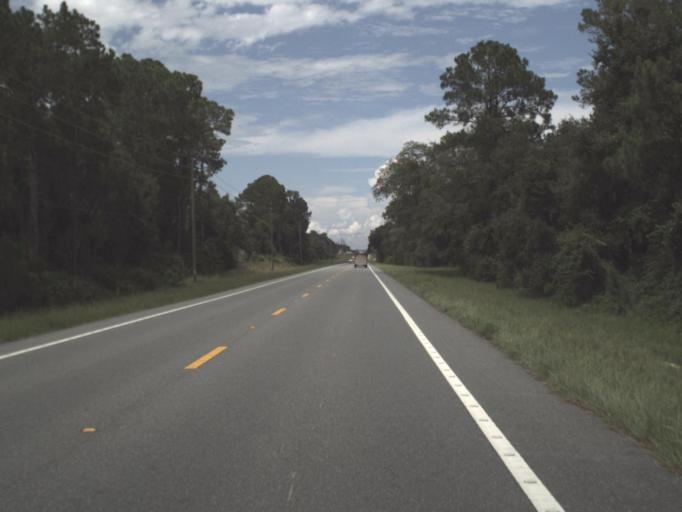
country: US
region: Florida
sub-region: Citrus County
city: Hernando
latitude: 28.9697
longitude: -82.3689
